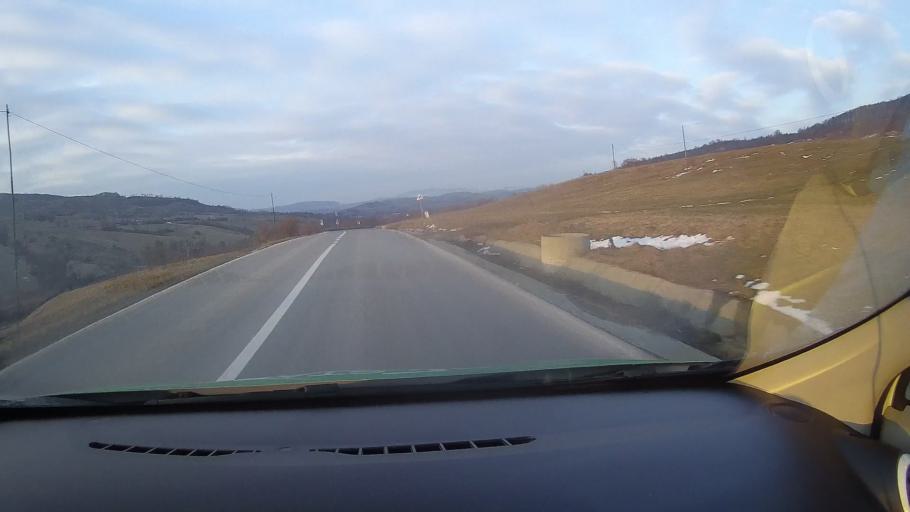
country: RO
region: Harghita
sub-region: Comuna Simonesti
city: Simonesti
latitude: 46.3213
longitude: 25.0994
